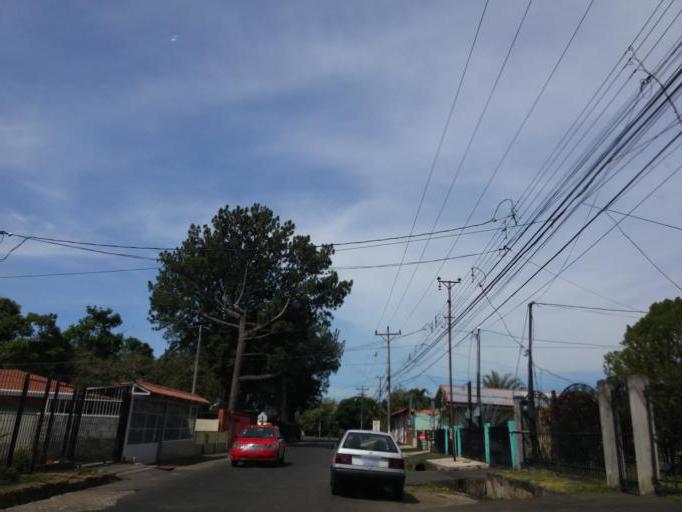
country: CR
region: Alajuela
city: Sabanilla
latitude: 10.0499
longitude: -84.2181
